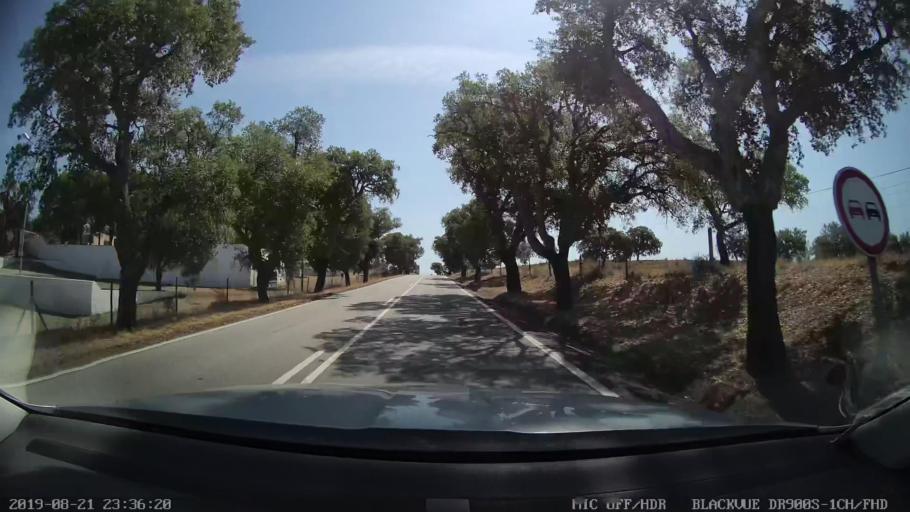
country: PT
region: Guarda
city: Alcains
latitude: 39.8764
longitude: -7.3765
